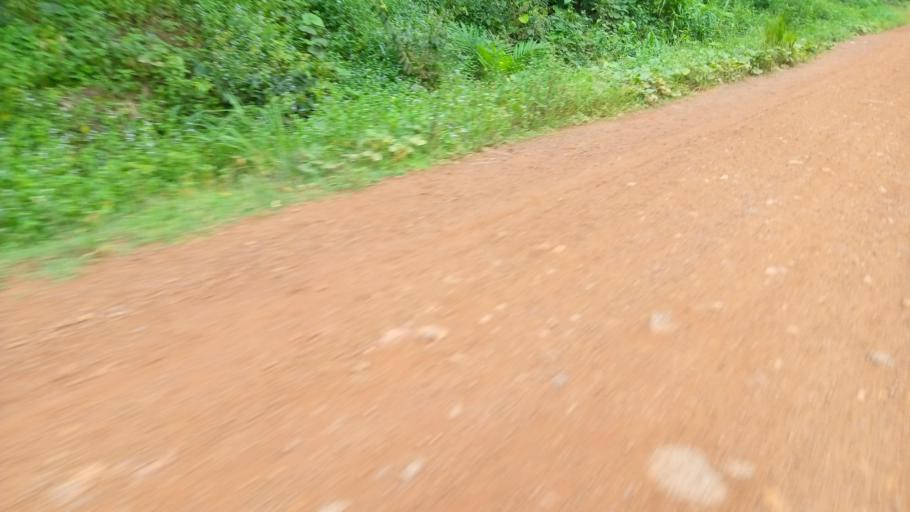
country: SL
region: Southern Province
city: Tongole
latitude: 7.4372
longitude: -11.8448
